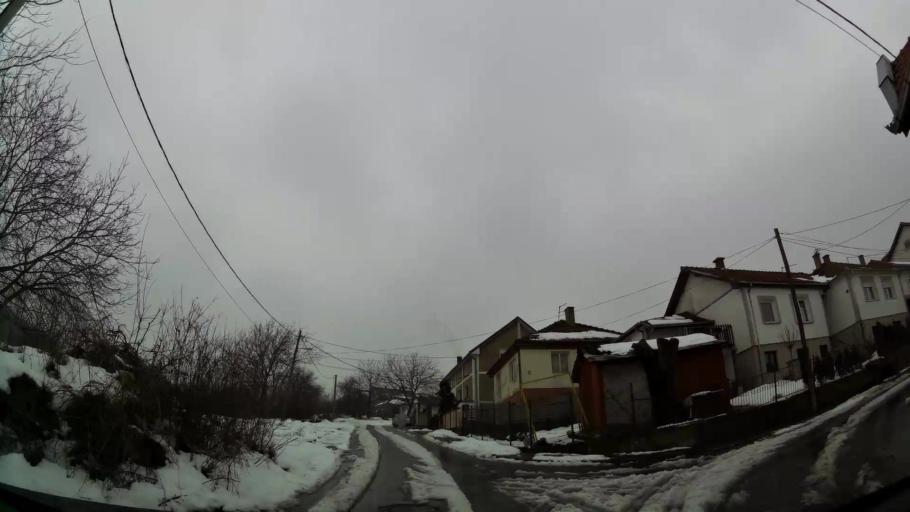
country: RS
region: Central Serbia
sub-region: Belgrade
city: Zvezdara
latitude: 44.7473
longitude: 20.5039
